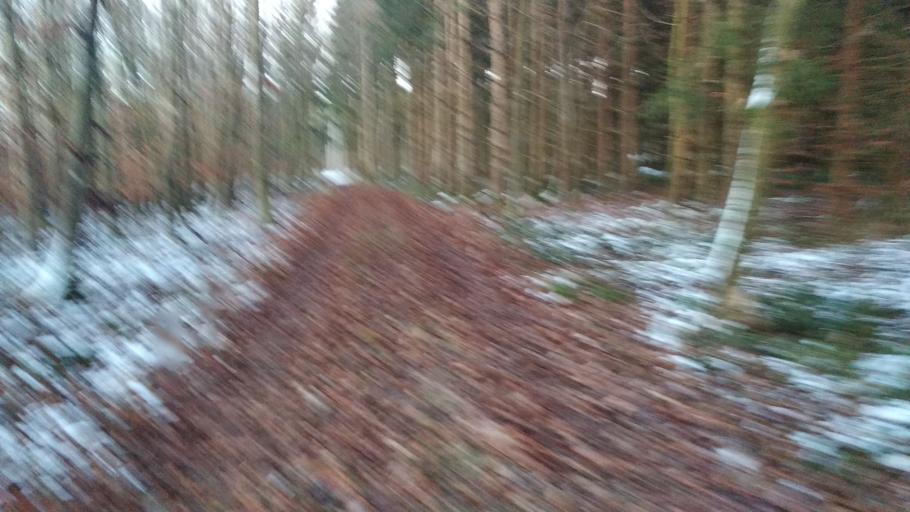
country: DE
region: Bavaria
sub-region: Upper Bavaria
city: Vaterstetten
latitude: 48.0708
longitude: 11.7854
